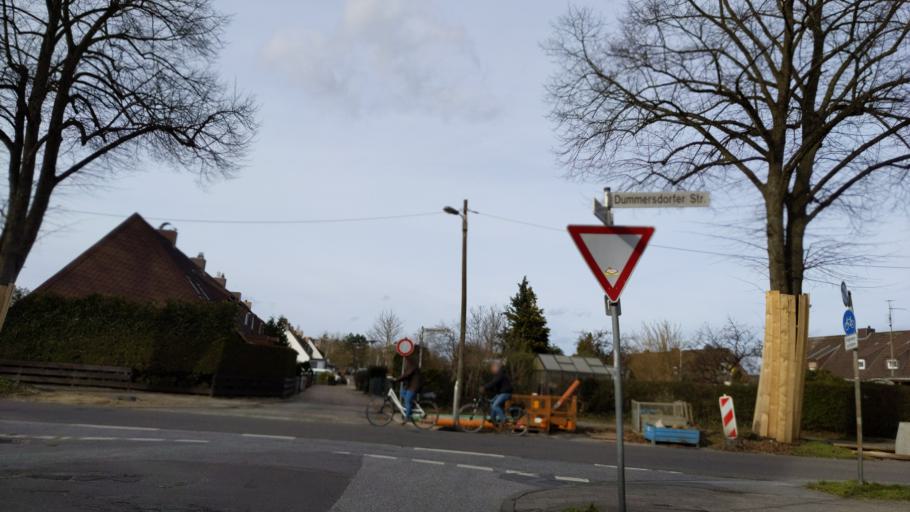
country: DE
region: Mecklenburg-Vorpommern
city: Selmsdorf
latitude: 53.9129
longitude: 10.8104
